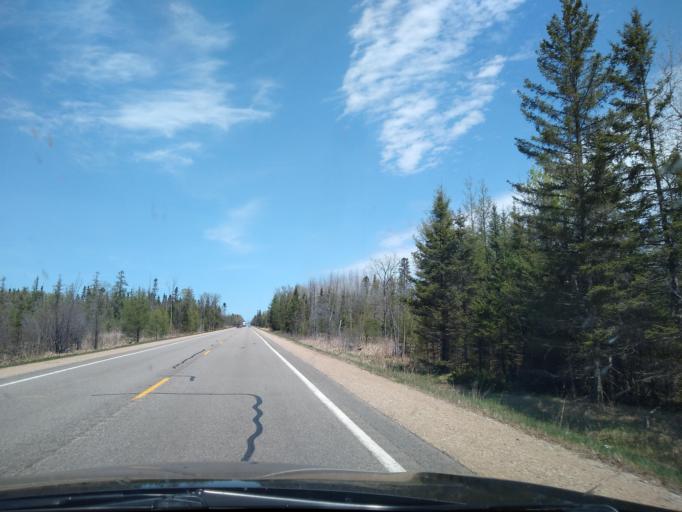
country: US
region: Michigan
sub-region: Delta County
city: Gladstone
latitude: 46.0543
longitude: -86.9813
